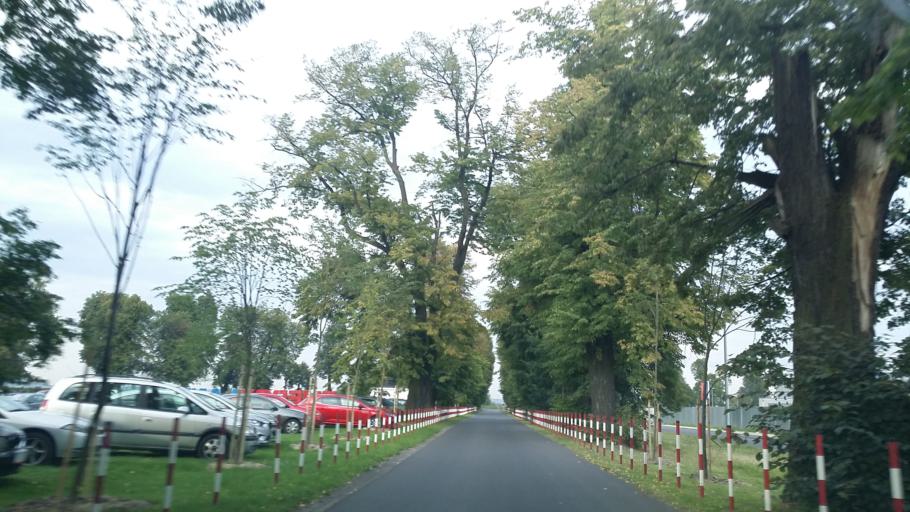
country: PL
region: Lesser Poland Voivodeship
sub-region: Powiat oswiecimski
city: Zator
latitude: 49.9981
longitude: 19.4149
